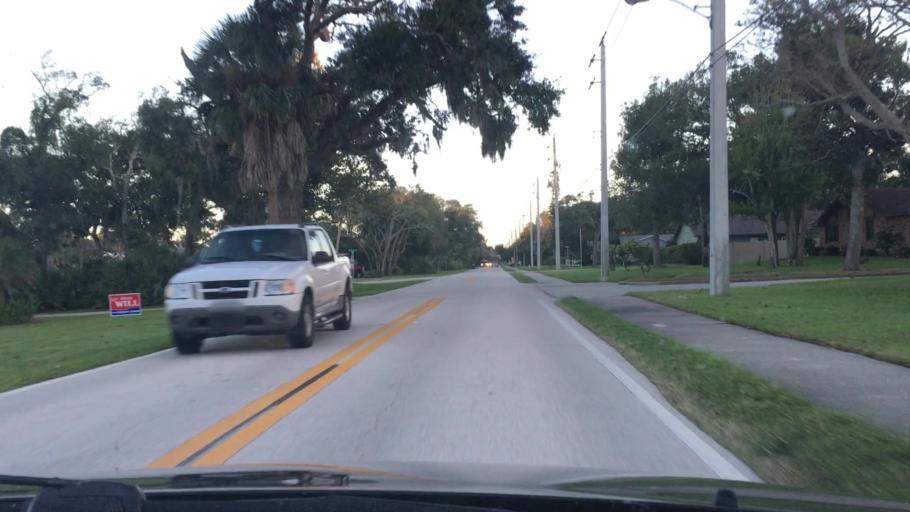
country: US
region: Florida
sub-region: Volusia County
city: Ormond Beach
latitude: 29.3146
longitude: -81.0702
